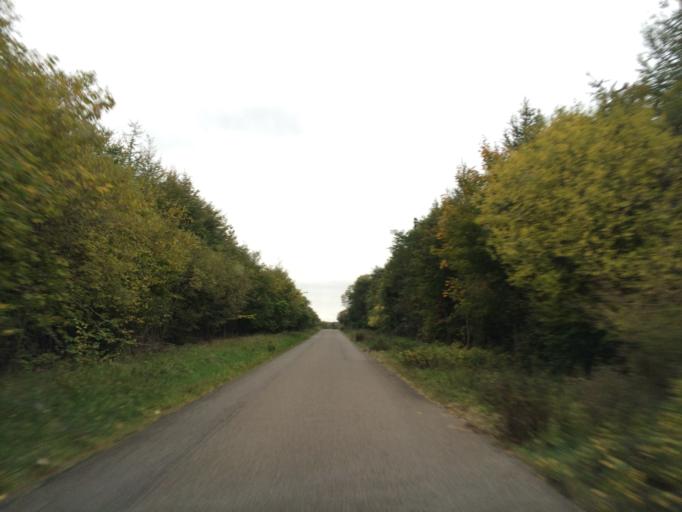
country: DK
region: Central Jutland
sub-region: Holstebro Kommune
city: Ulfborg
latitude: 56.2200
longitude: 8.4470
